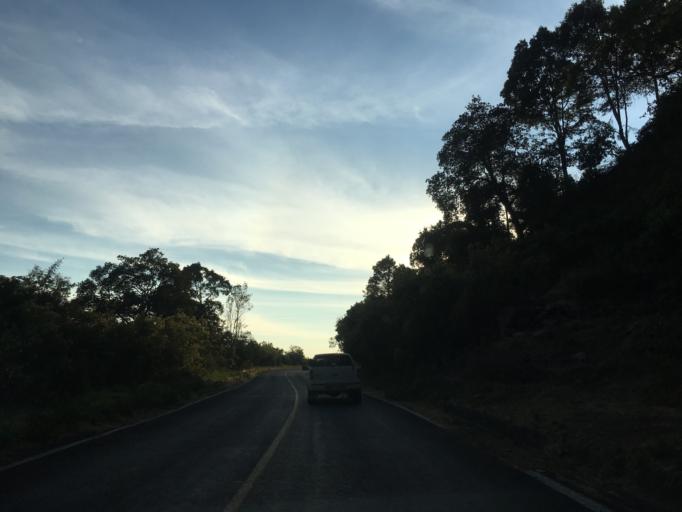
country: MX
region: Michoacan
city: Tzitzio
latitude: 19.6534
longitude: -100.9500
